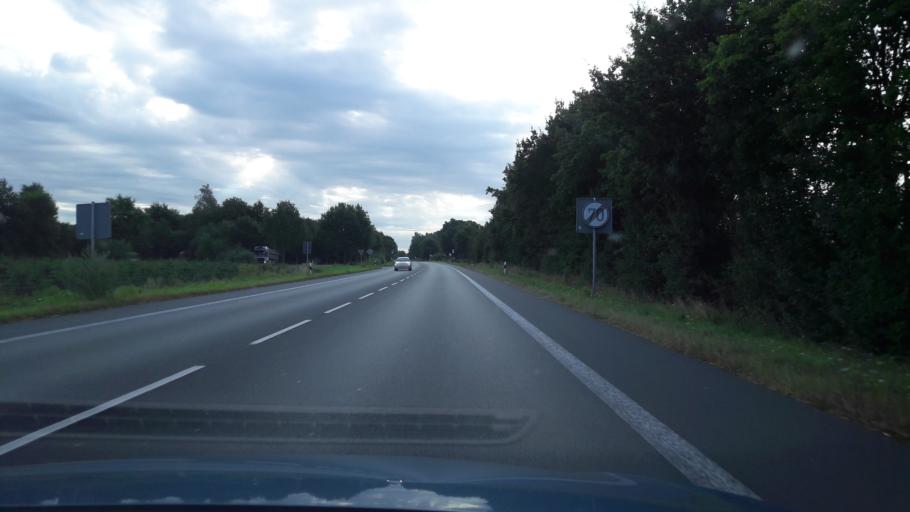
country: DE
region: North Rhine-Westphalia
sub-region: Regierungsbezirk Munster
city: Everswinkel
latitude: 51.9282
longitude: 7.8082
